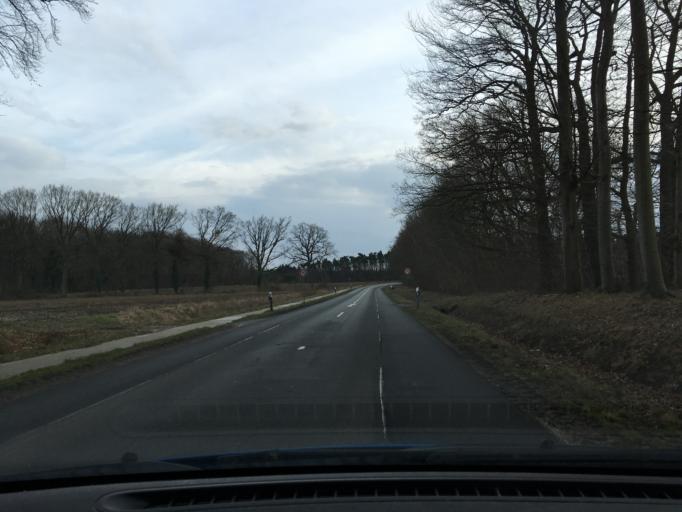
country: DE
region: Lower Saxony
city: Reppenstedt
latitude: 53.2641
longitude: 10.3405
